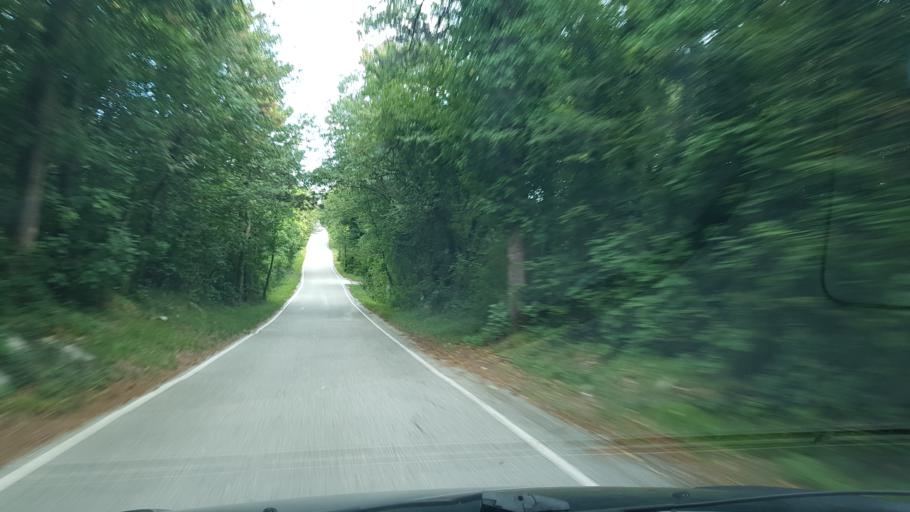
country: SI
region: Rence-Vogrsko
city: Rence
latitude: 45.8634
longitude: 13.6647
